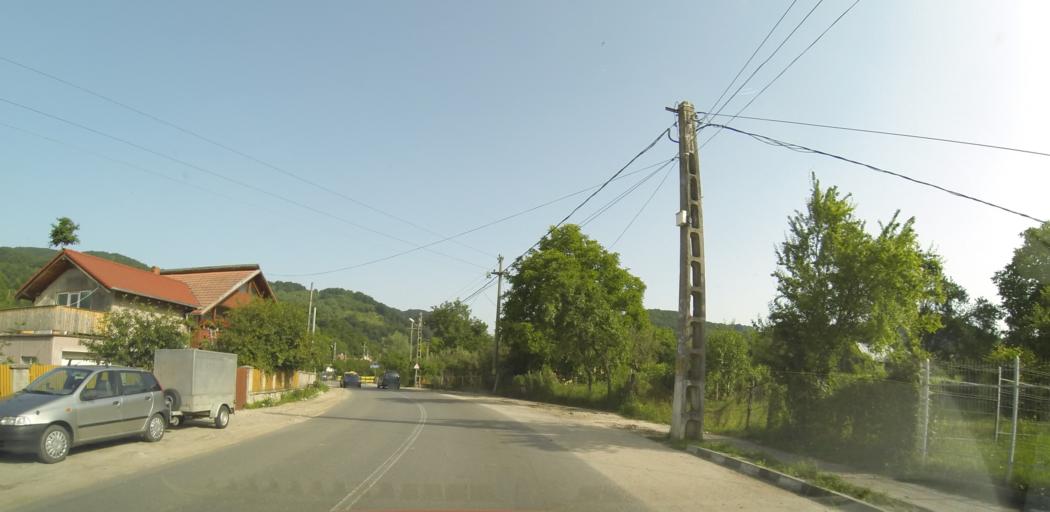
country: RO
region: Valcea
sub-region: Oras Baile Olanesti
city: Olanesti
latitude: 45.1821
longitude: 24.2573
